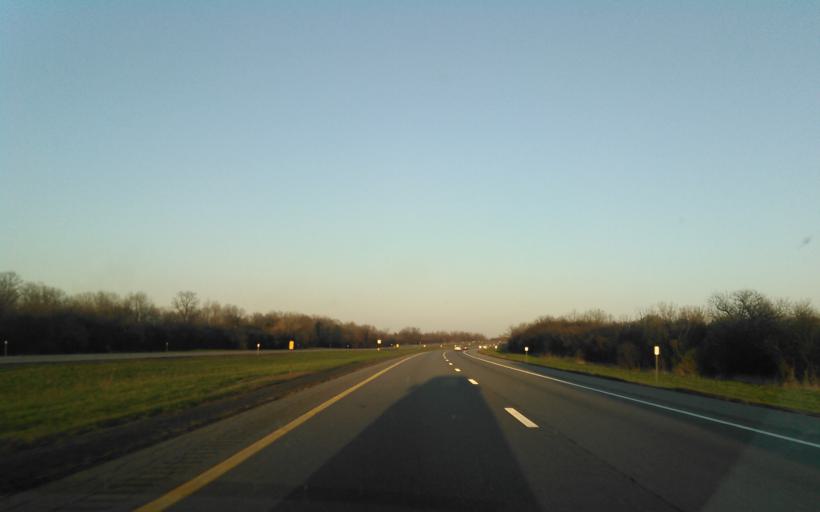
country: US
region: New York
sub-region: Ontario County
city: Phelps
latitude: 42.9736
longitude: -77.0893
